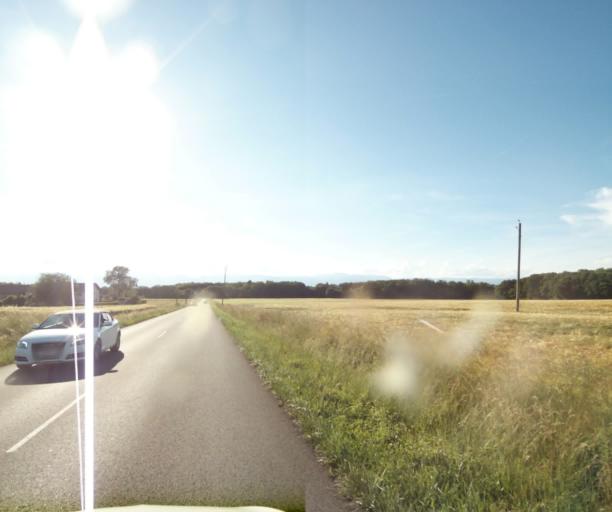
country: FR
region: Rhone-Alpes
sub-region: Departement de la Haute-Savoie
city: Loisin
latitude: 46.2681
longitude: 6.2944
